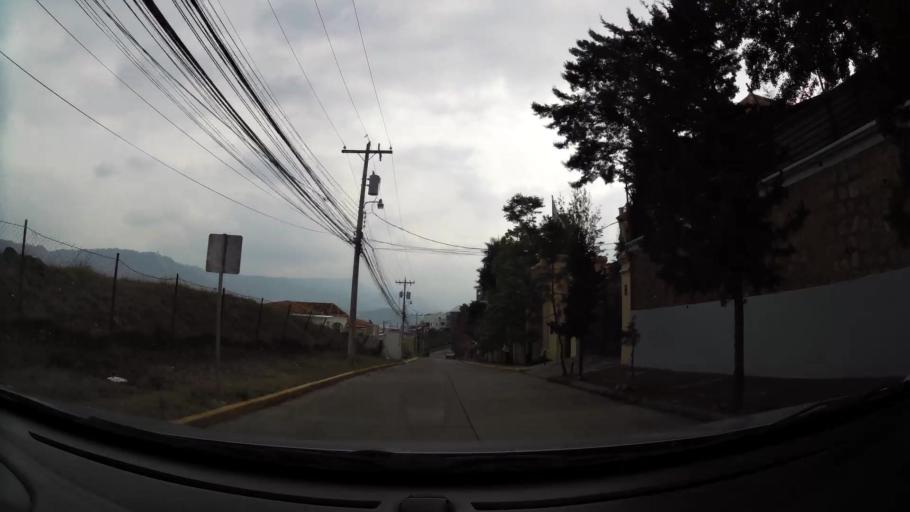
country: HN
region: Francisco Morazan
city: Tegucigalpa
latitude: 14.0932
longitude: -87.1875
